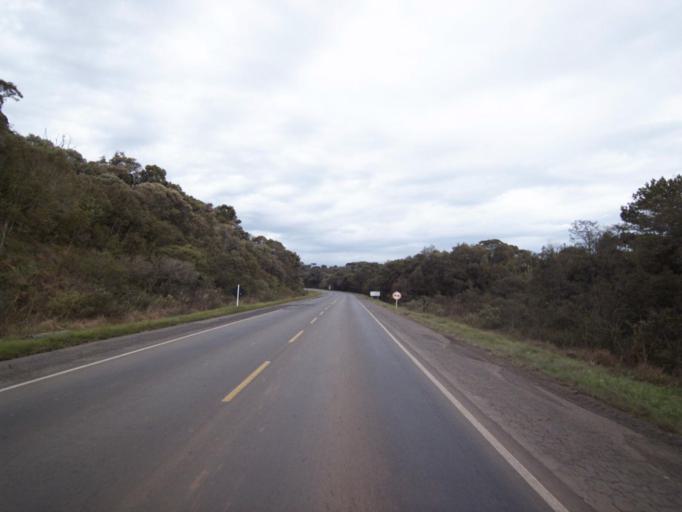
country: BR
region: Santa Catarina
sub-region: Concordia
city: Concordia
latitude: -26.9666
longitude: -51.8483
